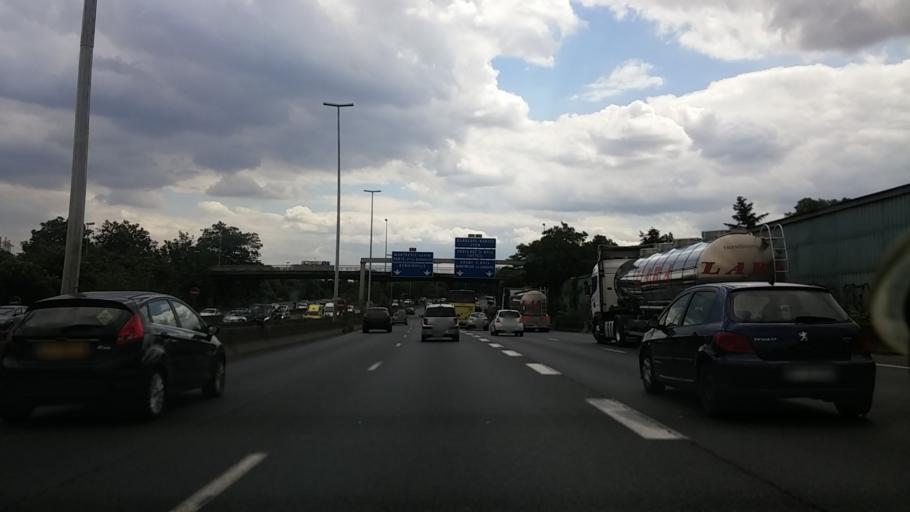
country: FR
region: Ile-de-France
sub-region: Departement de Seine-Saint-Denis
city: Noisy-le-Sec
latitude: 48.8902
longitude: 2.4735
